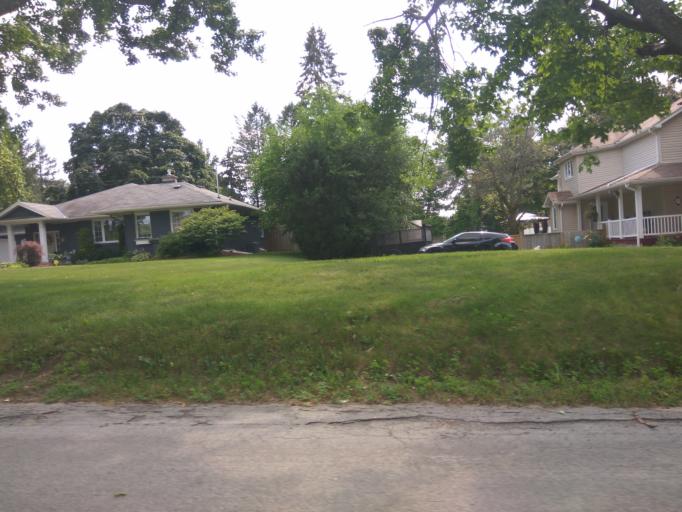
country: CA
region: Ontario
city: Cambridge
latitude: 43.4020
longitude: -80.3851
